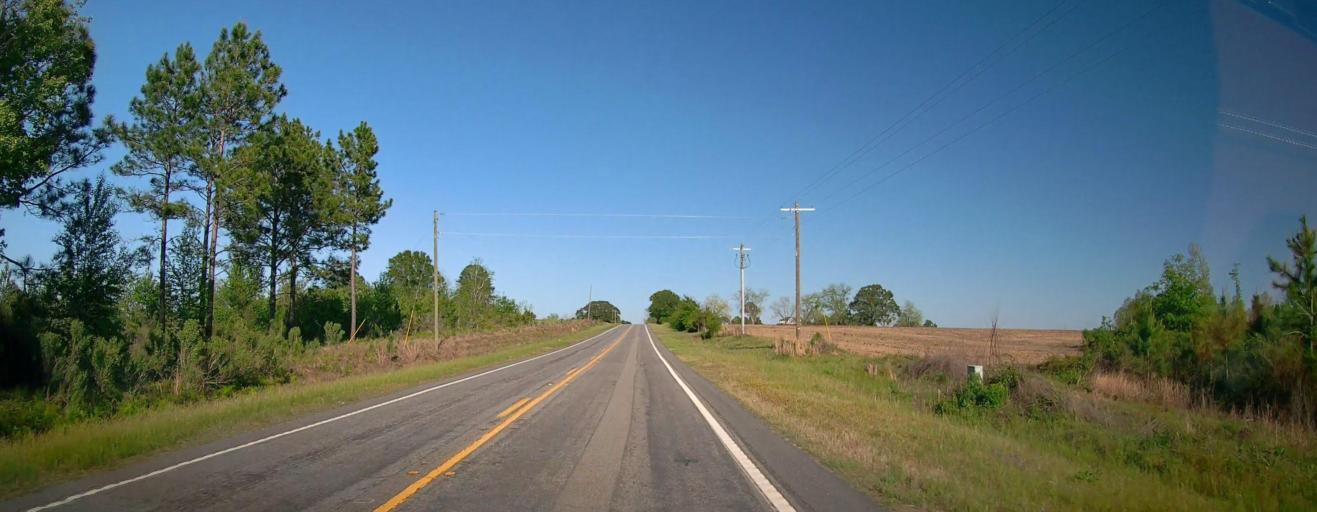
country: US
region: Georgia
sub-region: Ben Hill County
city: Fitzgerald
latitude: 31.7195
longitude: -83.3813
